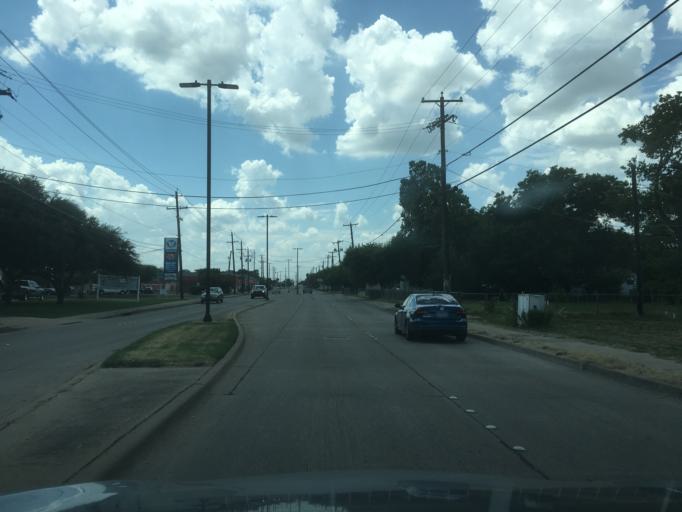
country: US
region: Texas
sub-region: Dallas County
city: Garland
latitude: 32.8790
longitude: -96.6526
